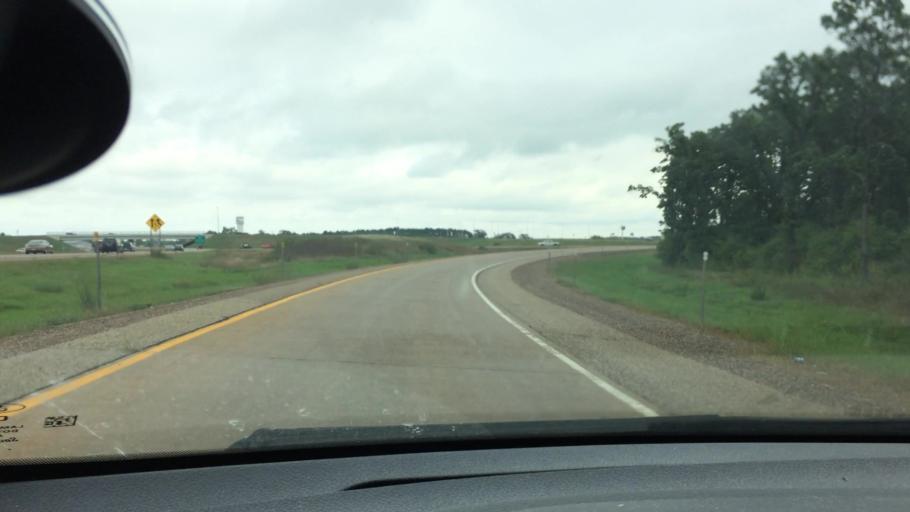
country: US
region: Wisconsin
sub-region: Chippewa County
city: Lake Hallie
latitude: 44.8783
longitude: -91.4171
